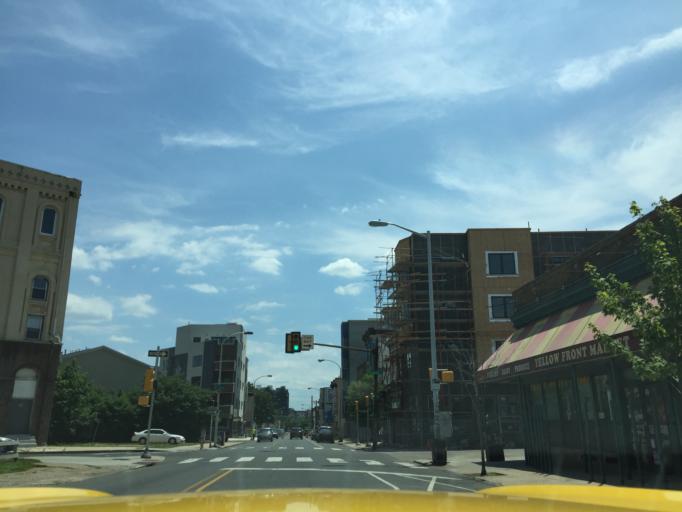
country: US
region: Pennsylvania
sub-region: Philadelphia County
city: Philadelphia
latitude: 39.9707
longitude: -75.1651
